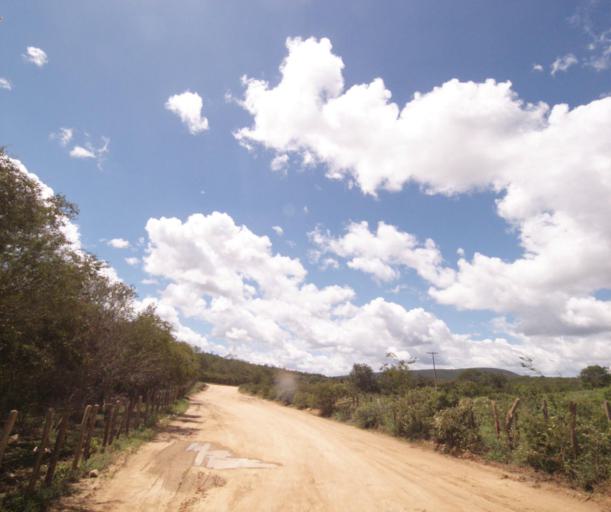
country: BR
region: Bahia
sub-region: Pocoes
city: Pocoes
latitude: -14.3788
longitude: -40.5648
